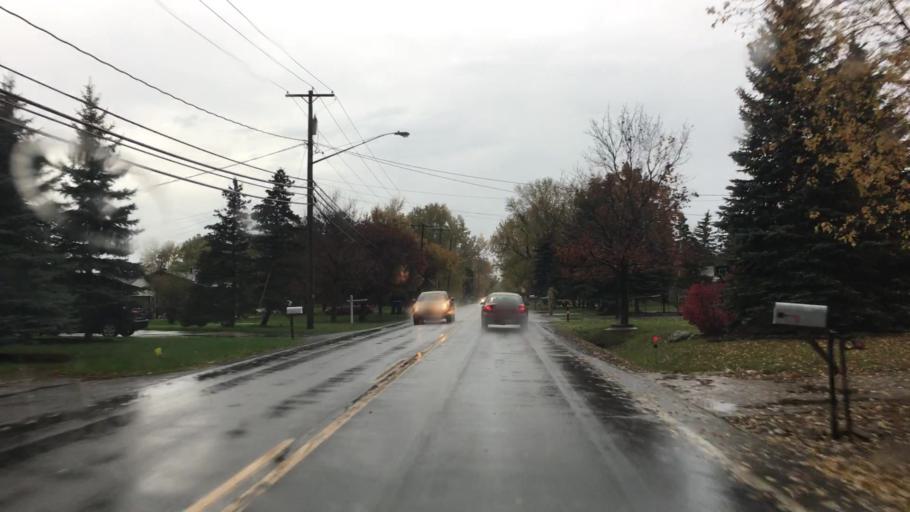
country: US
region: New York
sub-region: Erie County
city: Lancaster
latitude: 42.8734
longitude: -78.6765
